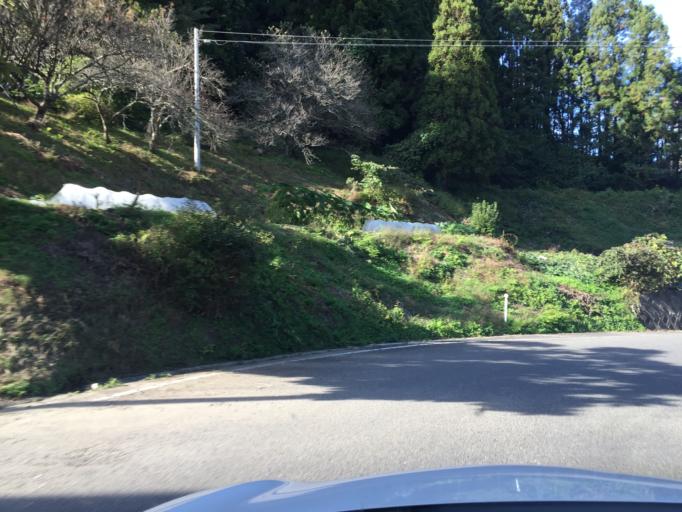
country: JP
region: Fukushima
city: Ishikawa
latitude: 37.1413
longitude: 140.5410
